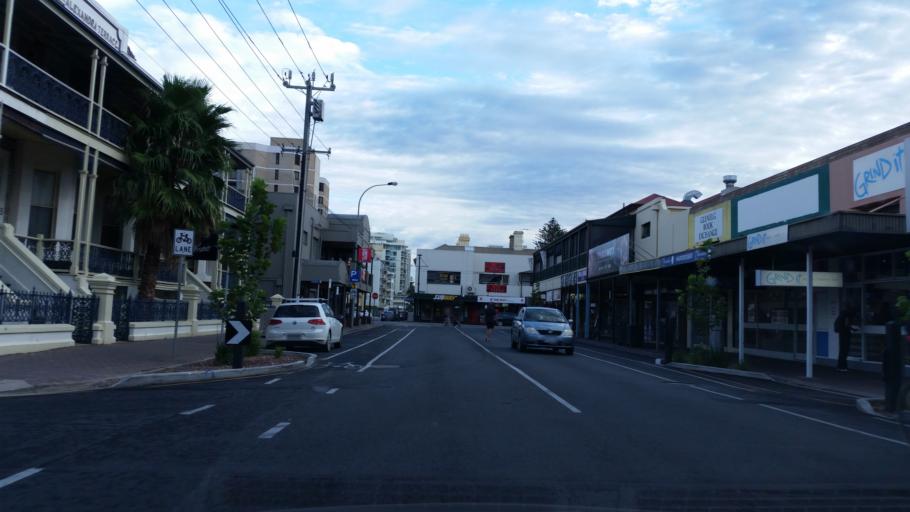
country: AU
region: South Australia
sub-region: Adelaide
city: Glenelg
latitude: -34.9811
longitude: 138.5132
